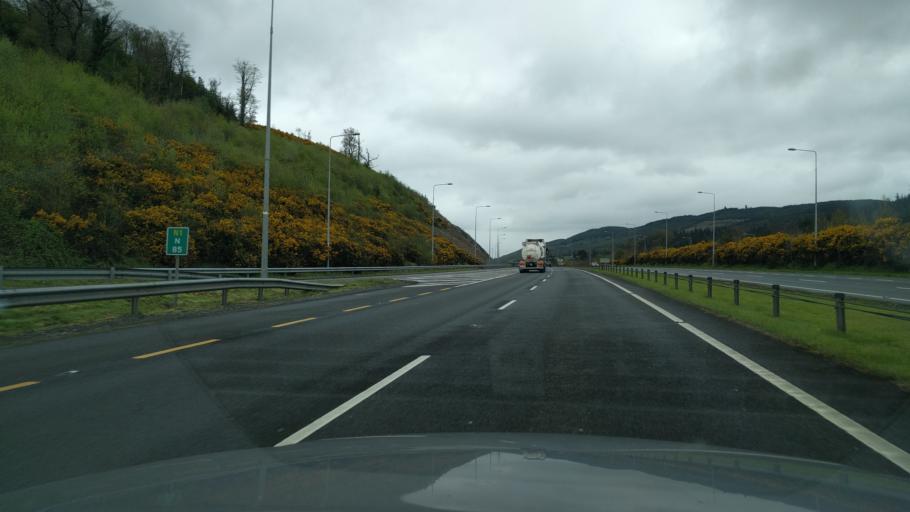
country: IE
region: Leinster
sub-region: Lu
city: Dundalk
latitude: 54.0684
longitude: -6.3512
